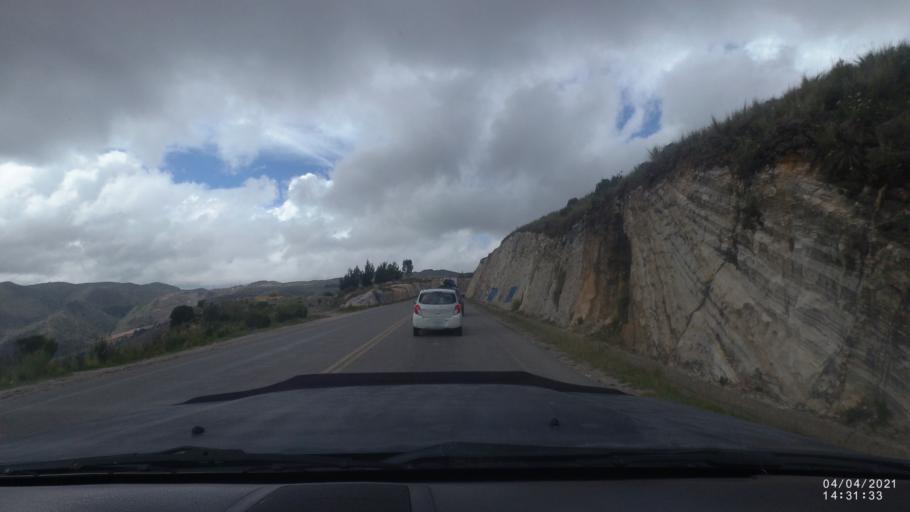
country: BO
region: Cochabamba
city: Irpa Irpa
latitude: -17.6985
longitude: -66.4927
